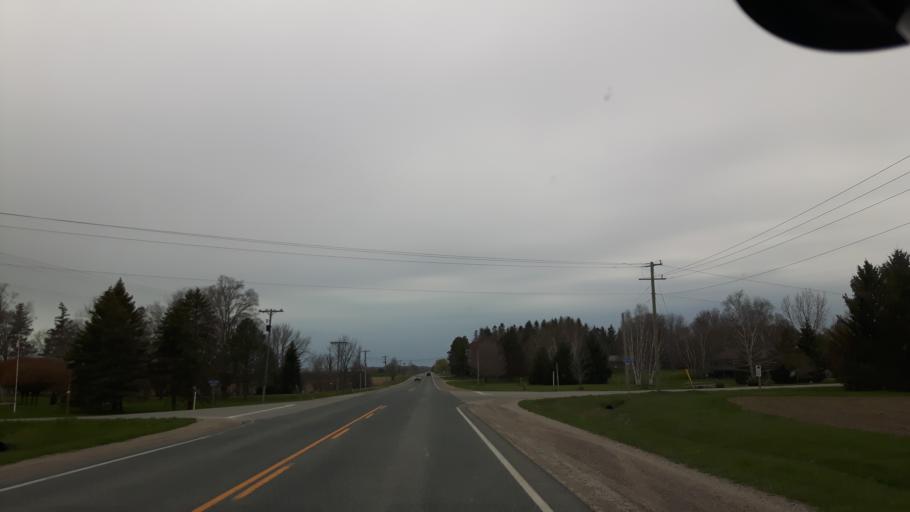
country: CA
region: Ontario
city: Bluewater
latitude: 43.6260
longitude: -81.5601
